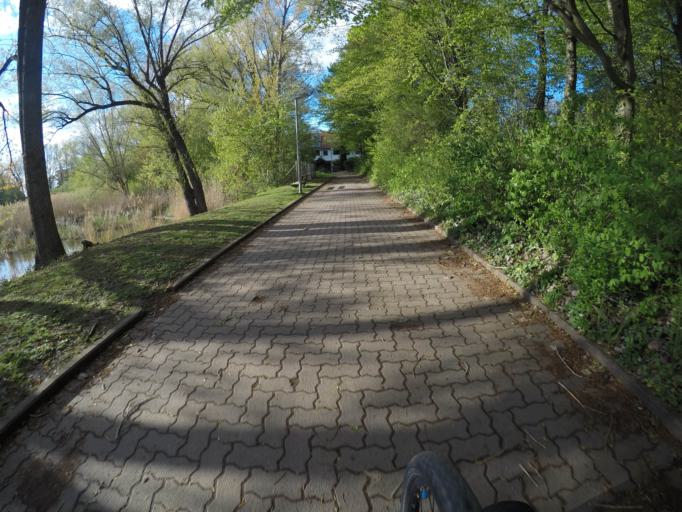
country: DE
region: Baden-Wuerttemberg
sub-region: Regierungsbezirk Stuttgart
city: Leinfelden-Echterdingen
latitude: 48.7295
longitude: 9.1395
